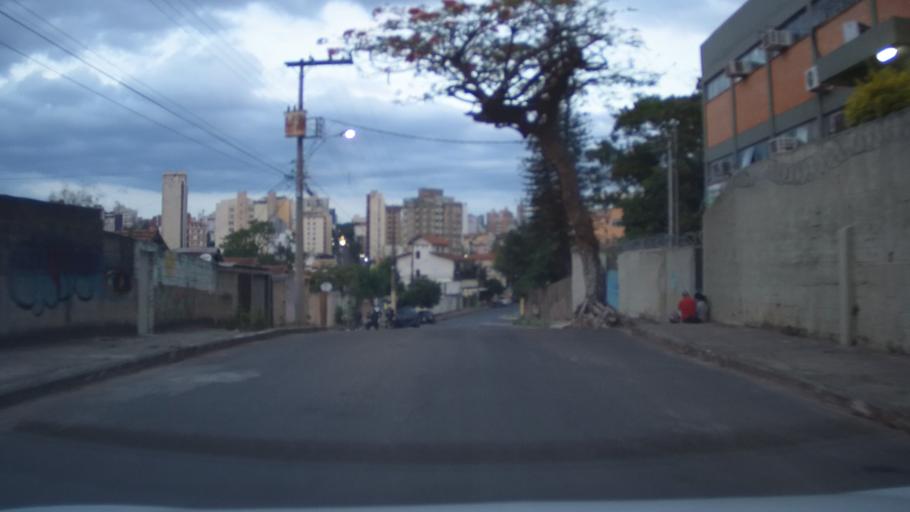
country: BR
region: Minas Gerais
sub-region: Belo Horizonte
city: Belo Horizonte
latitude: -19.8854
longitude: -43.9314
